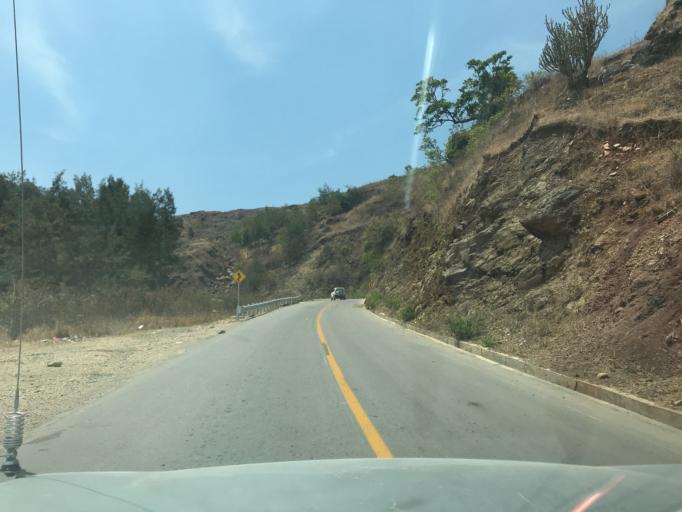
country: TL
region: Aileu
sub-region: Aileu Villa
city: Aileu
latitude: -8.8054
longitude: 125.5923
